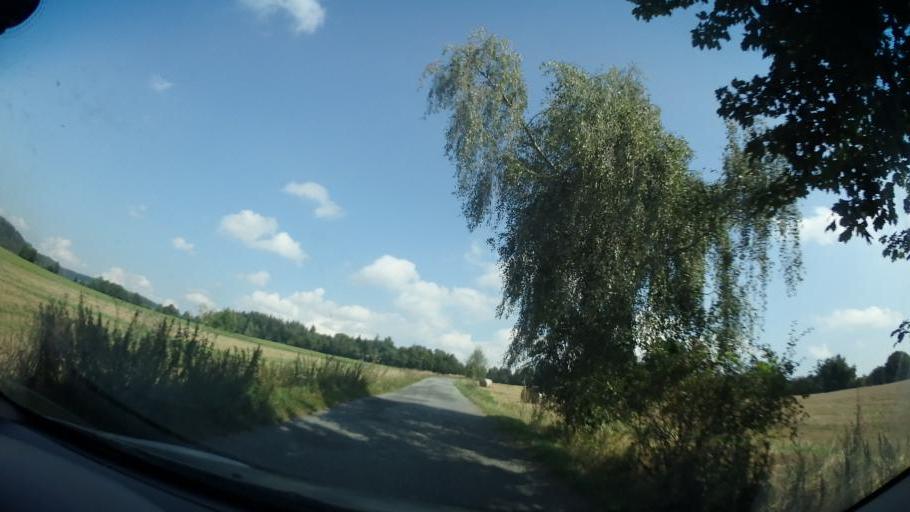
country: CZ
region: Pardubicky
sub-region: Okres Svitavy
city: Bystre
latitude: 49.5652
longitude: 16.3533
